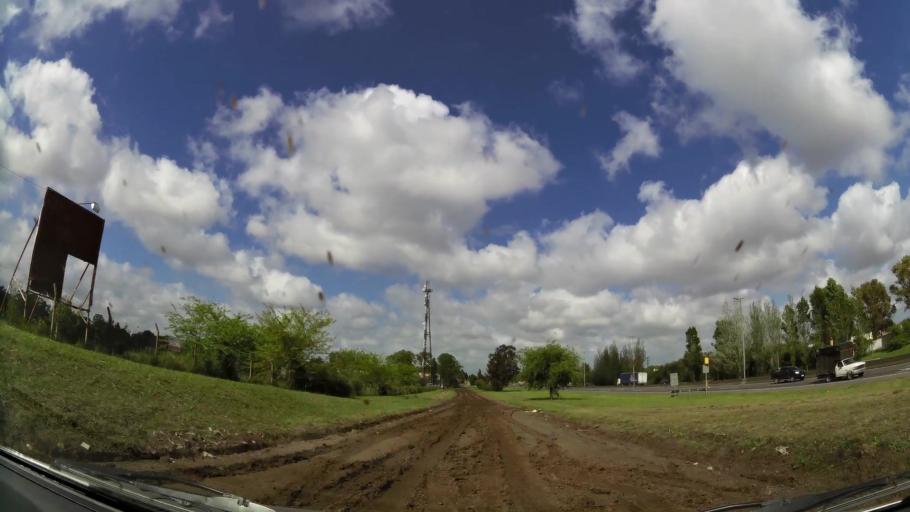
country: AR
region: Buenos Aires
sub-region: Partido de Quilmes
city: Quilmes
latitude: -34.8085
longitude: -58.1727
